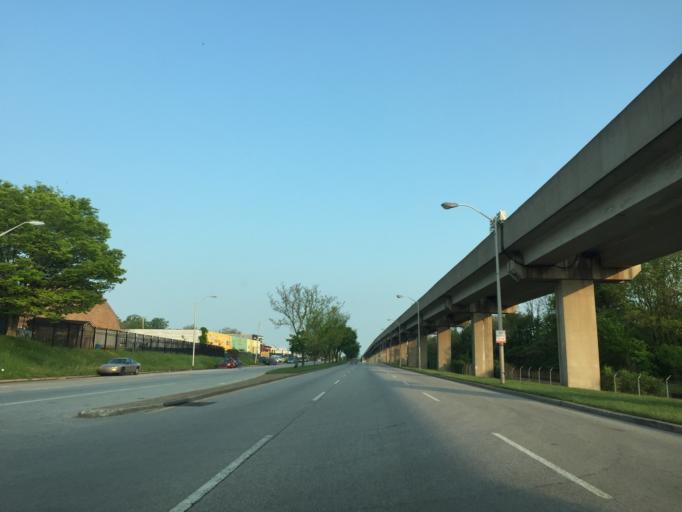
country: US
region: Maryland
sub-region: Baltimore County
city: Lochearn
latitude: 39.3397
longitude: -76.6780
